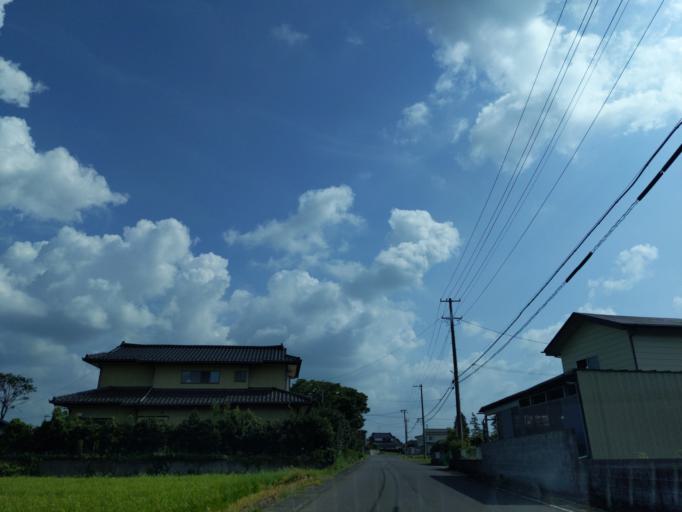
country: JP
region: Fukushima
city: Koriyama
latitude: 37.3449
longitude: 140.3264
